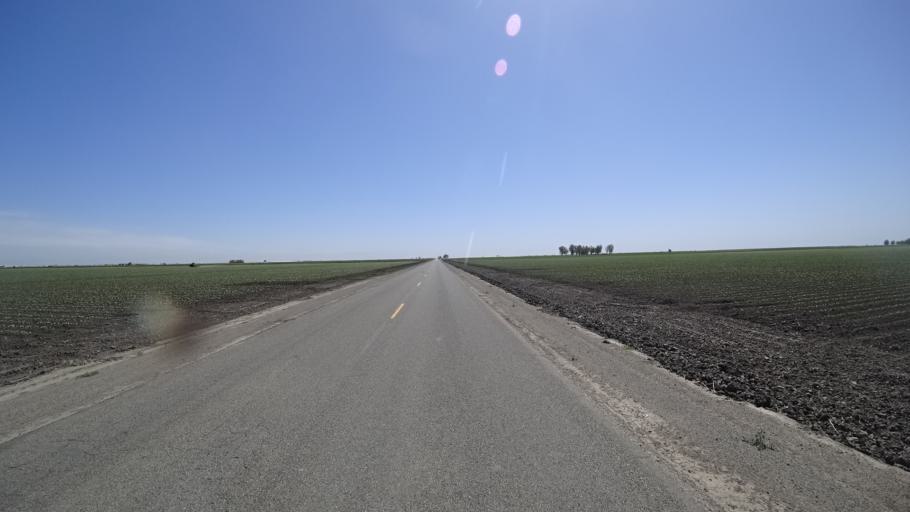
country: US
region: California
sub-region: Kings County
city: Stratford
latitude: 36.1894
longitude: -119.7755
